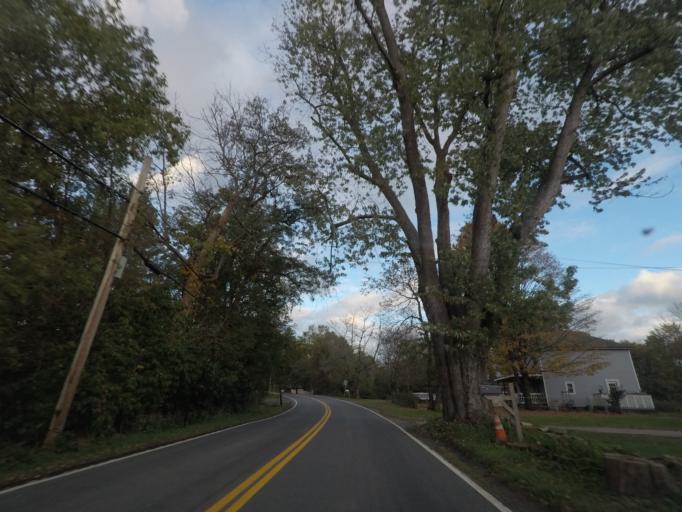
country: US
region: New York
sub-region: Rensselaer County
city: Nassau
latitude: 42.5574
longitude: -73.6288
